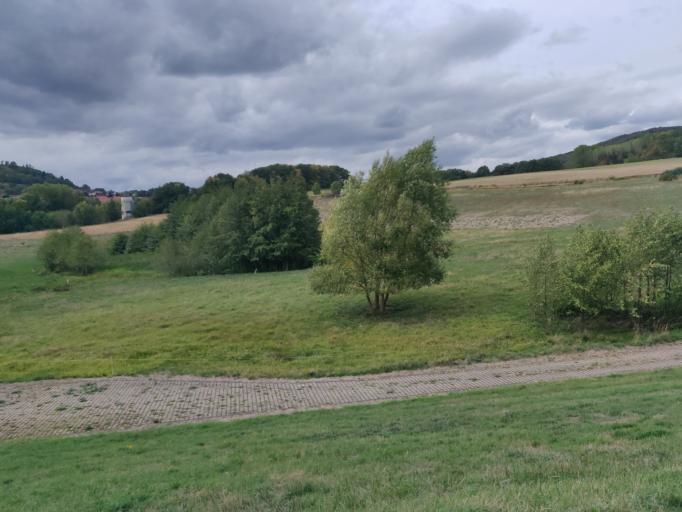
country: DE
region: Hesse
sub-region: Regierungsbezirk Kassel
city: Baunatal
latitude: 51.2821
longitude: 9.3596
